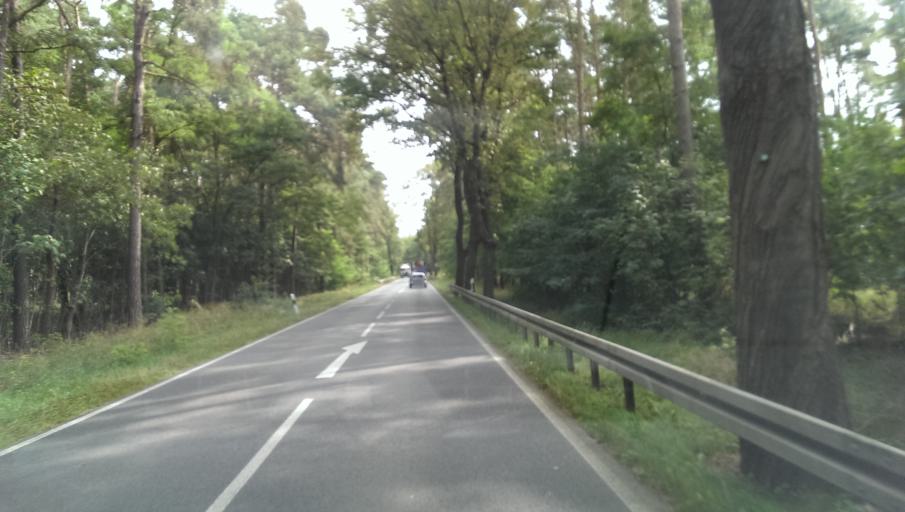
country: DE
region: Brandenburg
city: Am Mellensee
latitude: 52.2255
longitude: 13.3731
